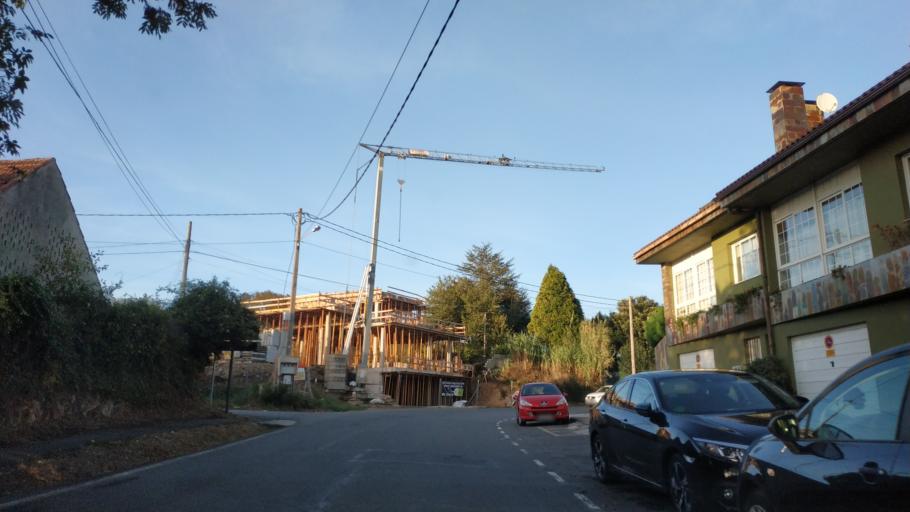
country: ES
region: Galicia
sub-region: Provincia da Coruna
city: Oleiros
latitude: 43.3627
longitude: -8.3413
